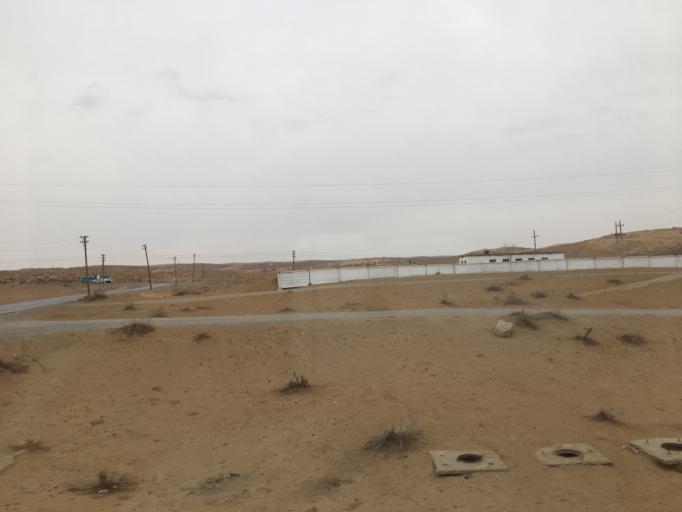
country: TM
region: Mary
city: Yoloeten
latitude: 36.4578
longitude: 62.5932
